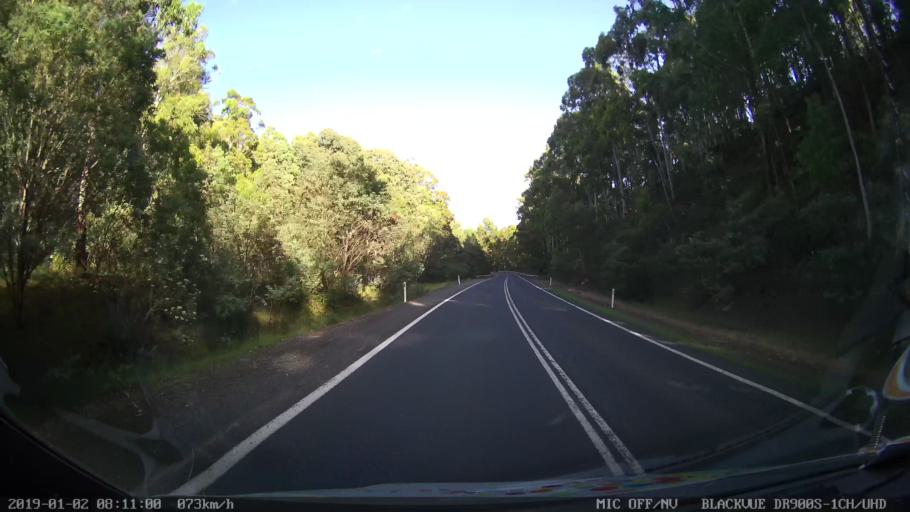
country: AU
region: New South Wales
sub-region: Tumut Shire
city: Tumut
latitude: -35.5984
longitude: 148.3631
